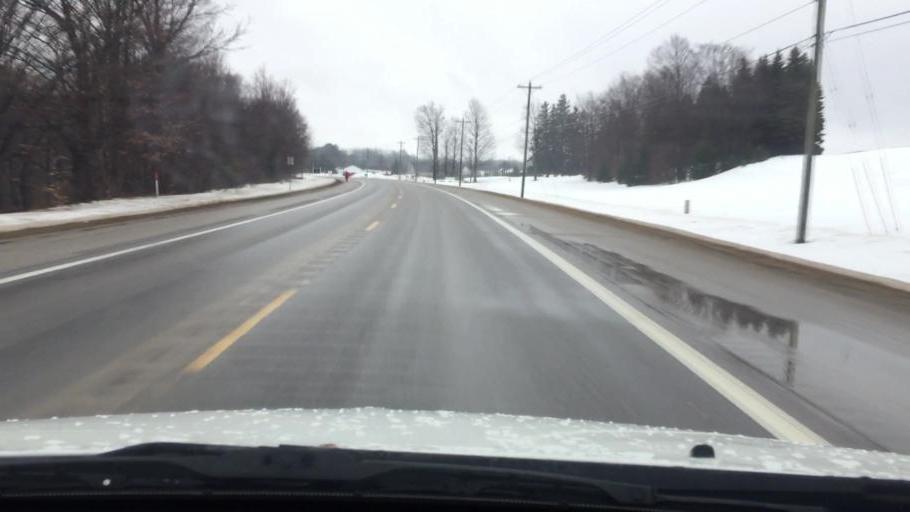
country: US
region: Michigan
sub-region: Charlevoix County
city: Charlevoix
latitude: 45.2841
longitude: -85.2411
